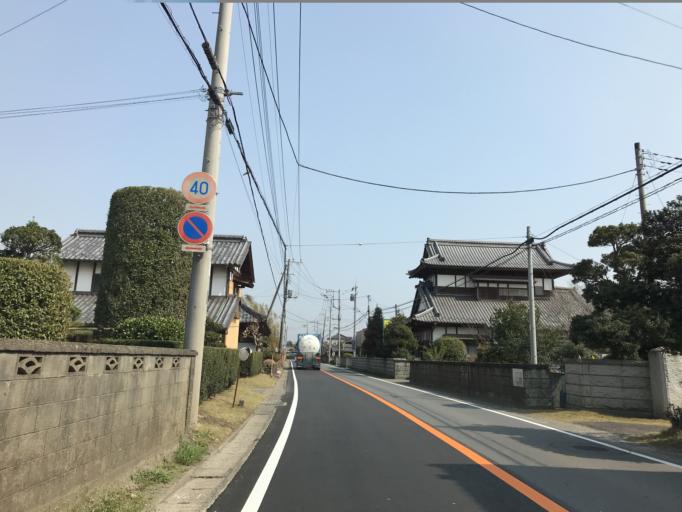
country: JP
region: Ibaraki
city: Tsukuba
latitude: 36.1486
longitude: 140.1562
